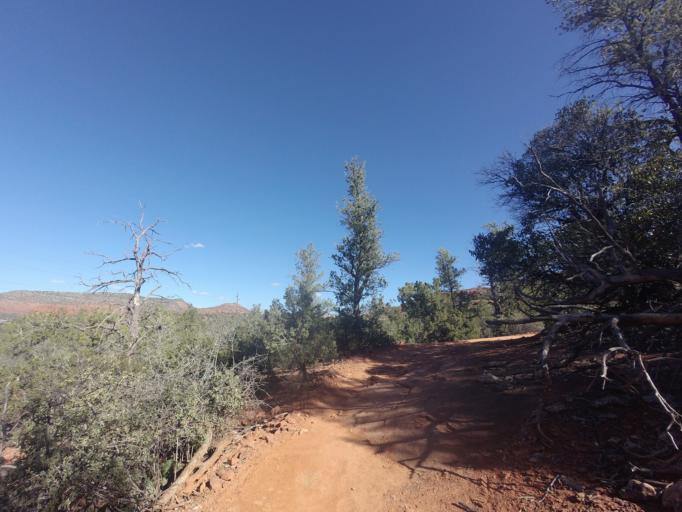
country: US
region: Arizona
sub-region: Yavapai County
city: West Sedona
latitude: 34.8158
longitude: -111.8075
